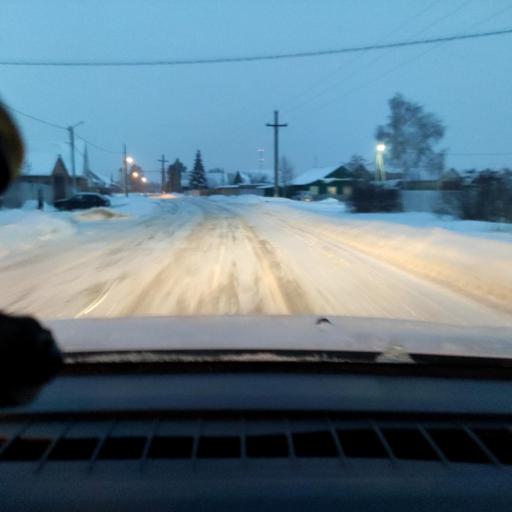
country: RU
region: Samara
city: Kinel'-Cherkassy
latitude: 53.4600
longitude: 51.5241
